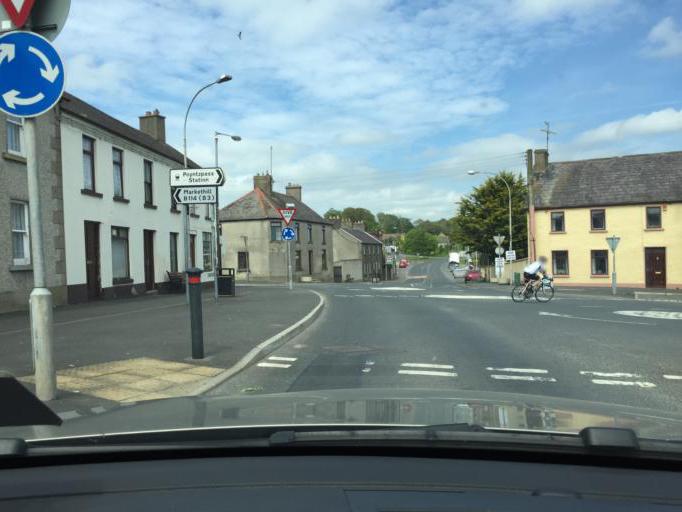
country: GB
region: Northern Ireland
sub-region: Armagh District
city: Tandragee
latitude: 54.2929
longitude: -6.3752
